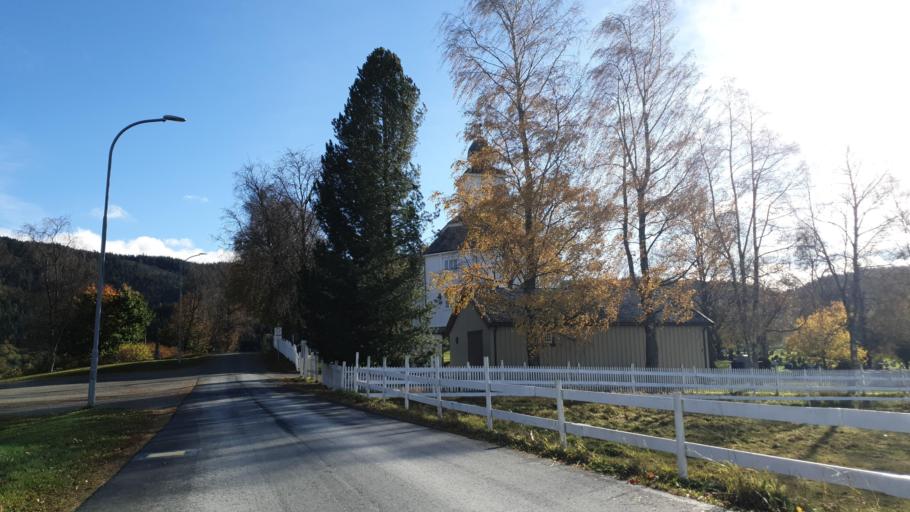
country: NO
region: Sor-Trondelag
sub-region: Klaebu
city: Klaebu
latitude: 63.2958
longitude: 10.4755
